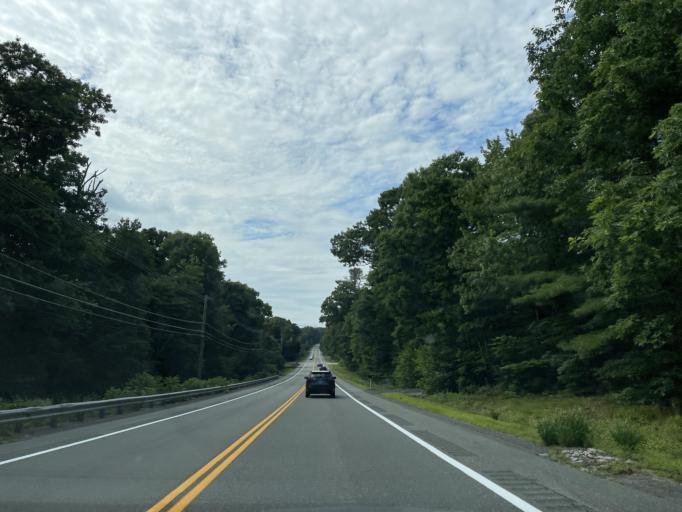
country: US
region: Rhode Island
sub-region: Kent County
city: West Greenwich
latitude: 41.6234
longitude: -71.6772
